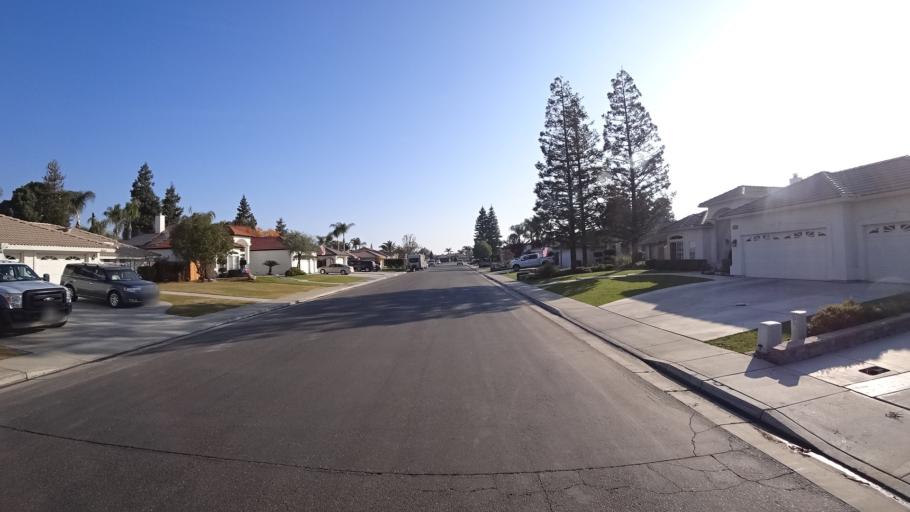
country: US
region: California
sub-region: Kern County
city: Greenacres
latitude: 35.3649
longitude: -119.1218
